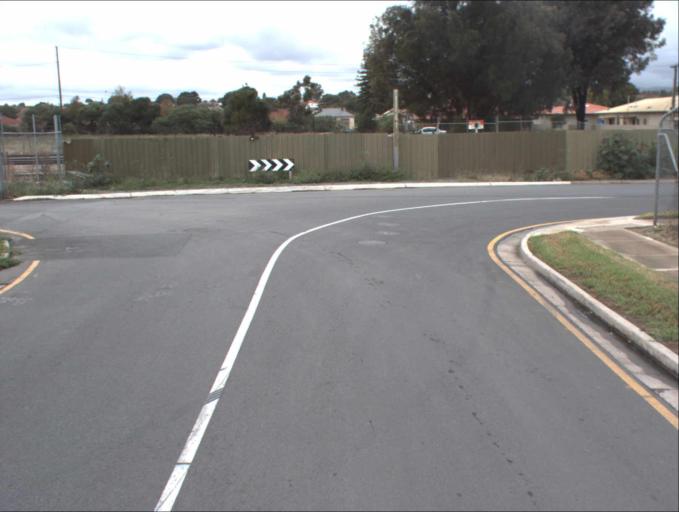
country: AU
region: South Australia
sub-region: Prospect
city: Prospect
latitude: -34.8782
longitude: 138.5823
